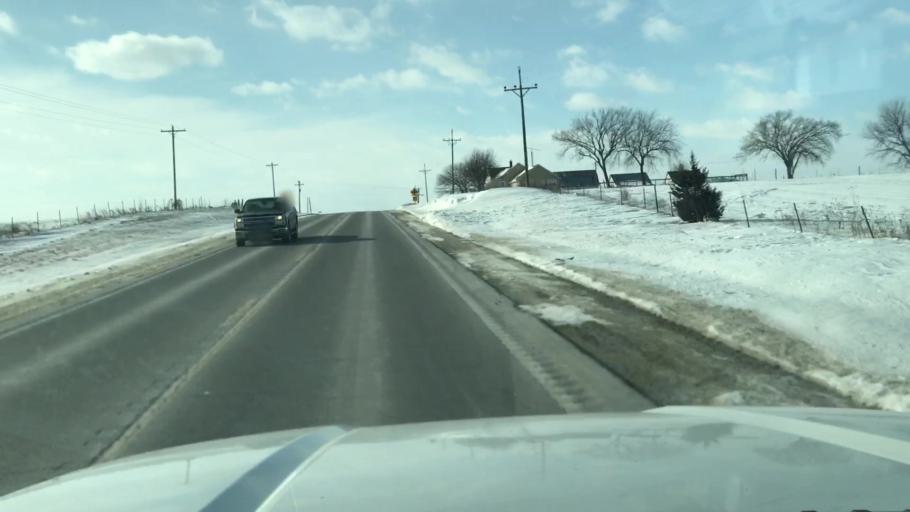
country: US
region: Missouri
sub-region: Nodaway County
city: Maryville
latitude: 40.3442
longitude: -94.7575
